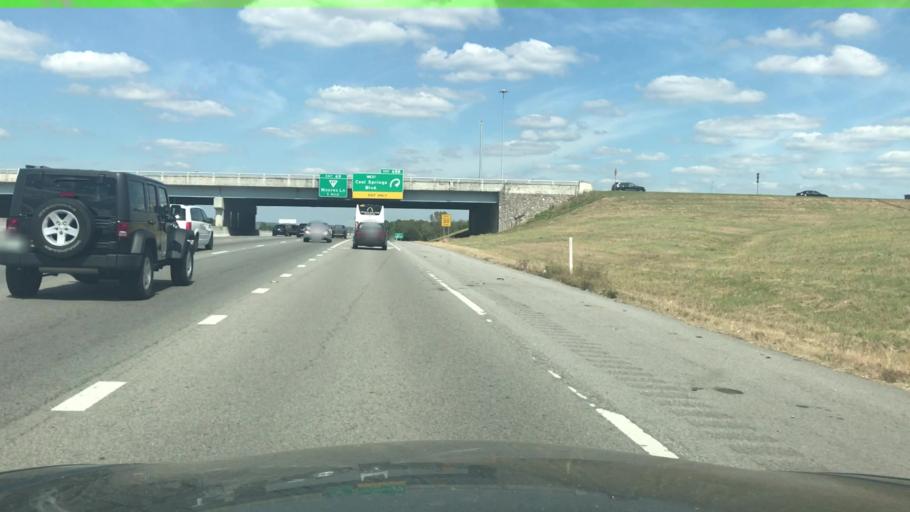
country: US
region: Tennessee
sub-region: Williamson County
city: Franklin
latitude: 35.9464
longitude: -86.8143
